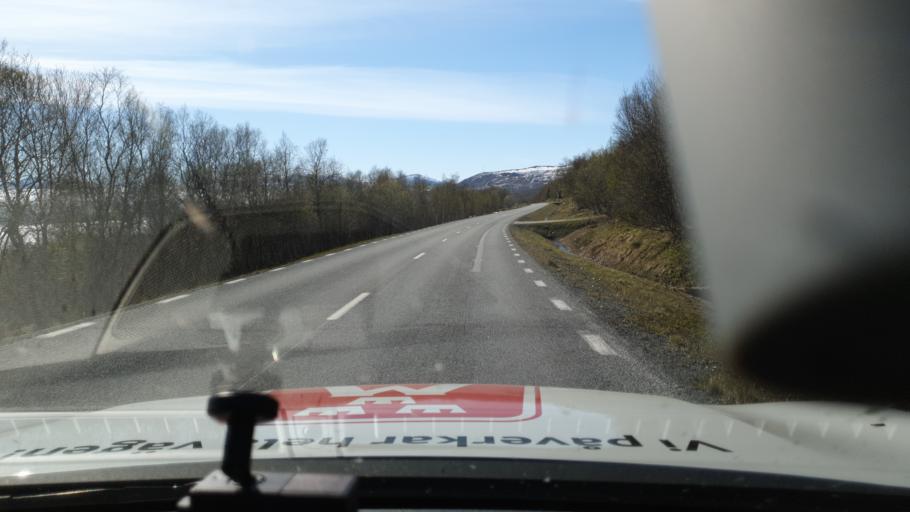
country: NO
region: Nordland
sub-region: Rana
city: Mo i Rana
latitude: 66.0419
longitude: 14.9936
